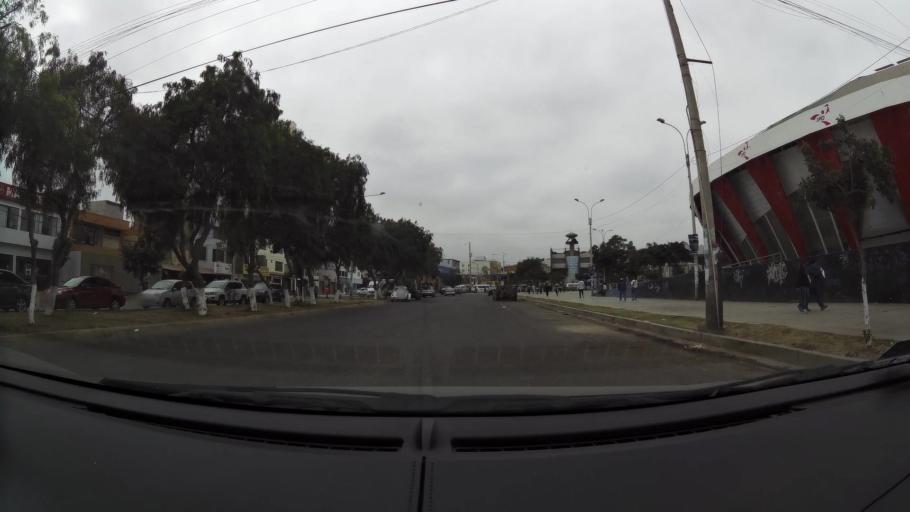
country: PE
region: La Libertad
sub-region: Provincia de Trujillo
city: Trujillo
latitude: -8.1048
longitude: -79.0321
